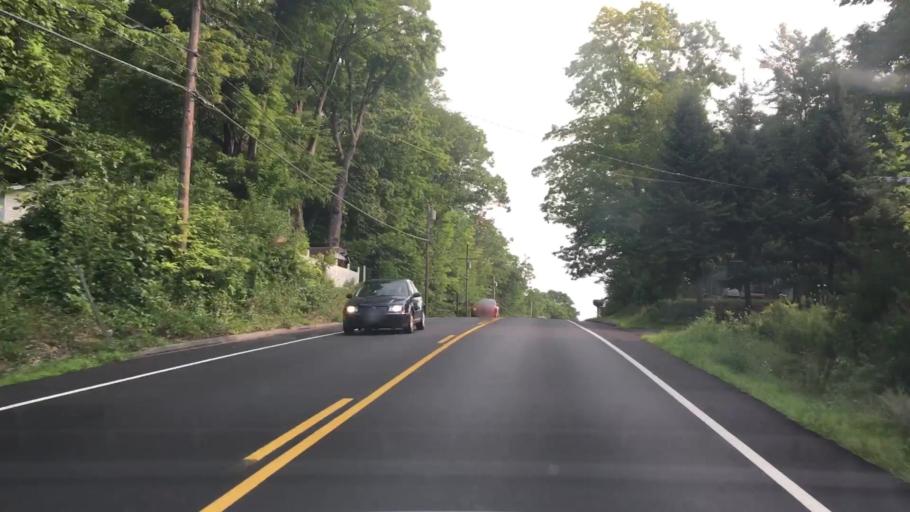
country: US
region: Maine
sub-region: Kennebec County
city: Chelsea
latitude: 44.2550
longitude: -69.7126
